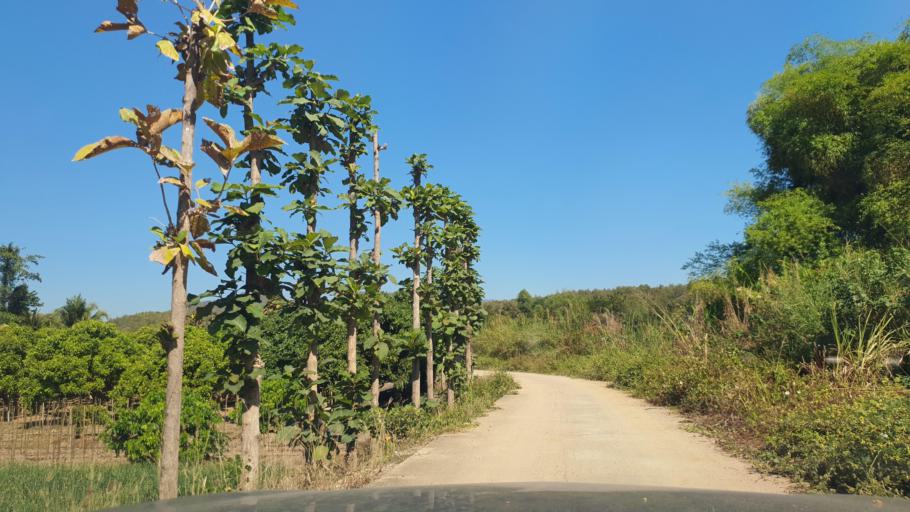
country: TH
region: Chiang Mai
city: San Pa Tong
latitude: 18.6673
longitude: 98.8313
